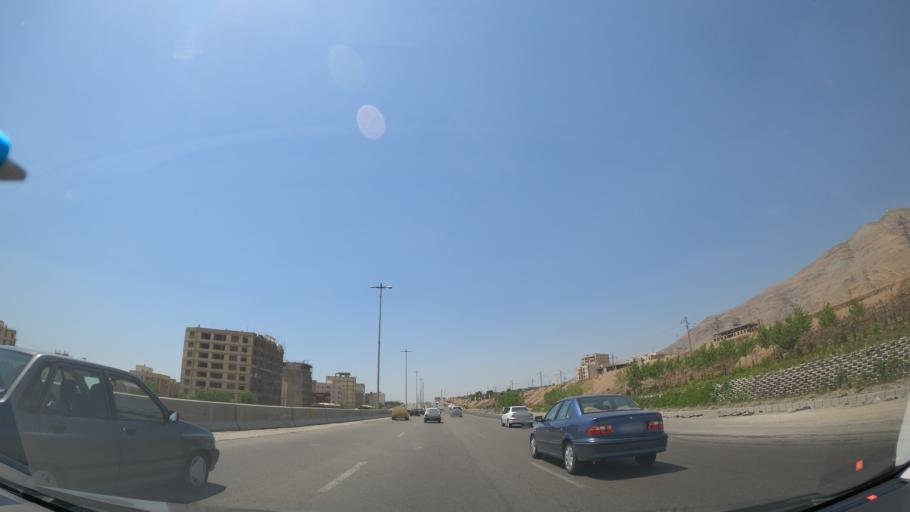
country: IR
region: Tehran
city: Shahr-e Qods
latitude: 35.7549
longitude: 51.0738
